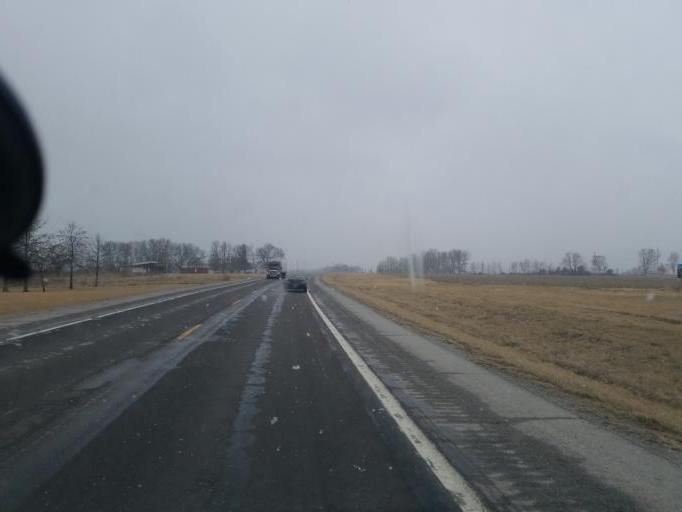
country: US
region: Missouri
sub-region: Schuyler County
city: Lancaster
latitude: 40.4064
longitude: -92.5596
